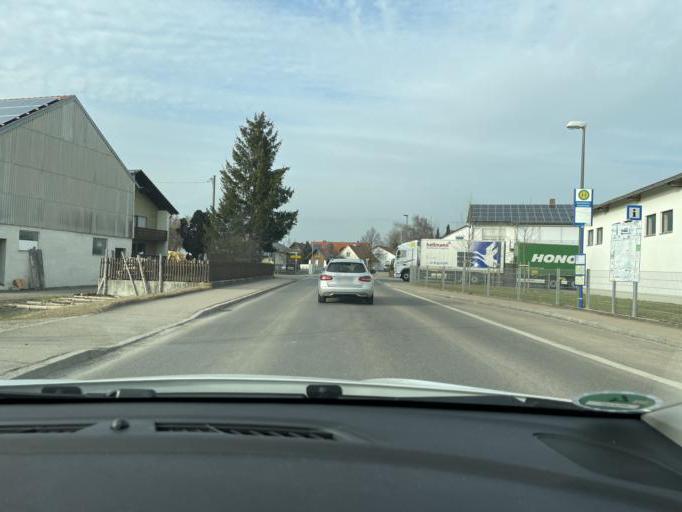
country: DE
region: Bavaria
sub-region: Swabia
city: Hollenbach
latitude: 48.4887
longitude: 11.0927
